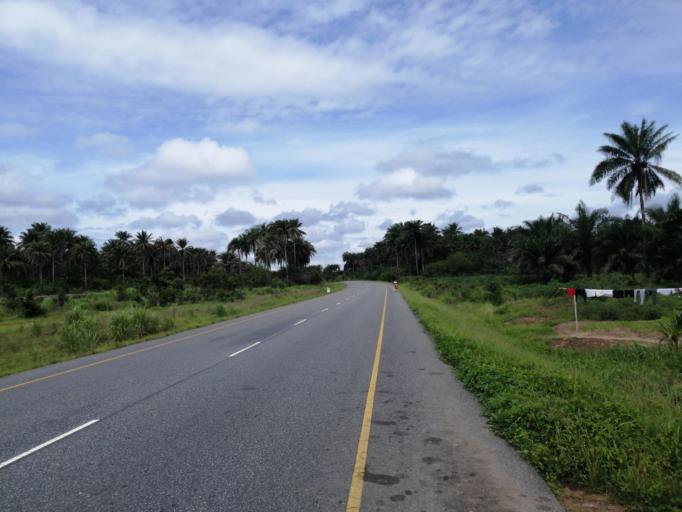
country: SL
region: Northern Province
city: Pepel
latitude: 8.7207
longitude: -12.9591
